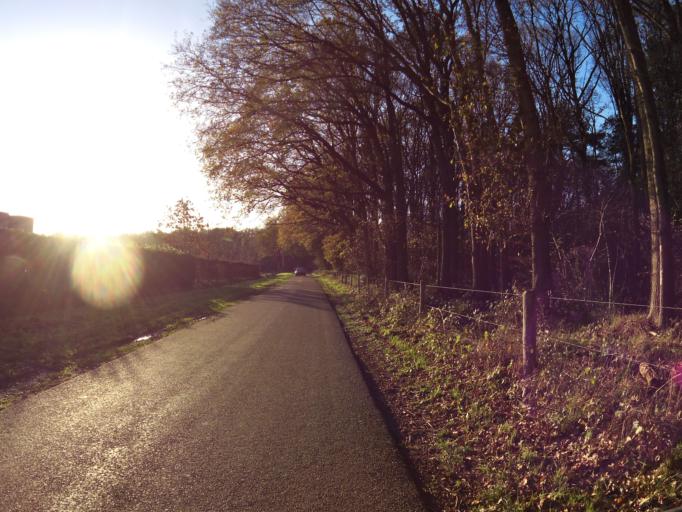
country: NL
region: North Brabant
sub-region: Gemeente Heusden
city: Heusden
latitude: 51.6651
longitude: 5.1436
